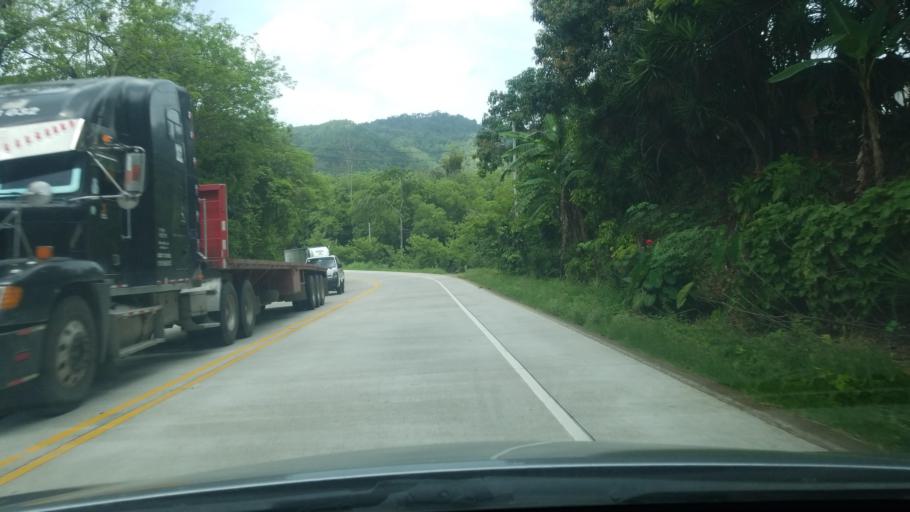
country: HN
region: Copan
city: San Juan de Planes
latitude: 14.9355
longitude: -88.7649
